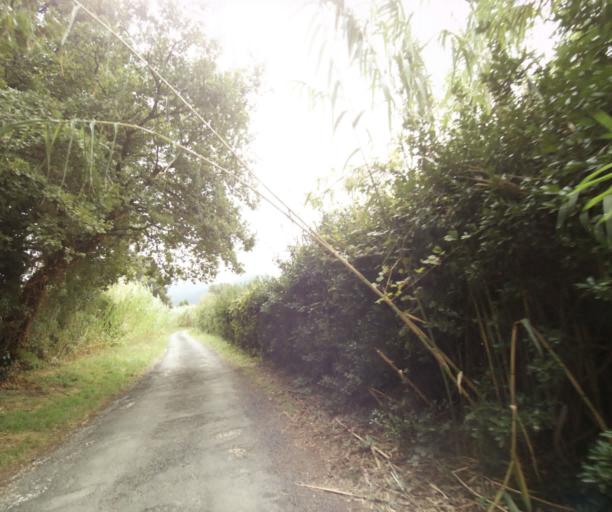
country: FR
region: Languedoc-Roussillon
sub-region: Departement des Pyrenees-Orientales
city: Argelers
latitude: 42.5536
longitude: 3.0338
